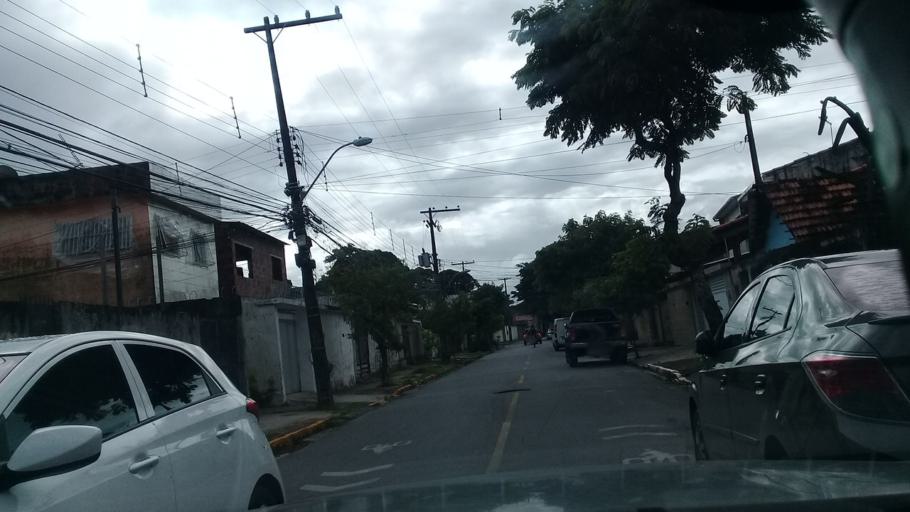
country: BR
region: Pernambuco
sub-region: Recife
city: Recife
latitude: -8.0344
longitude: -34.8833
